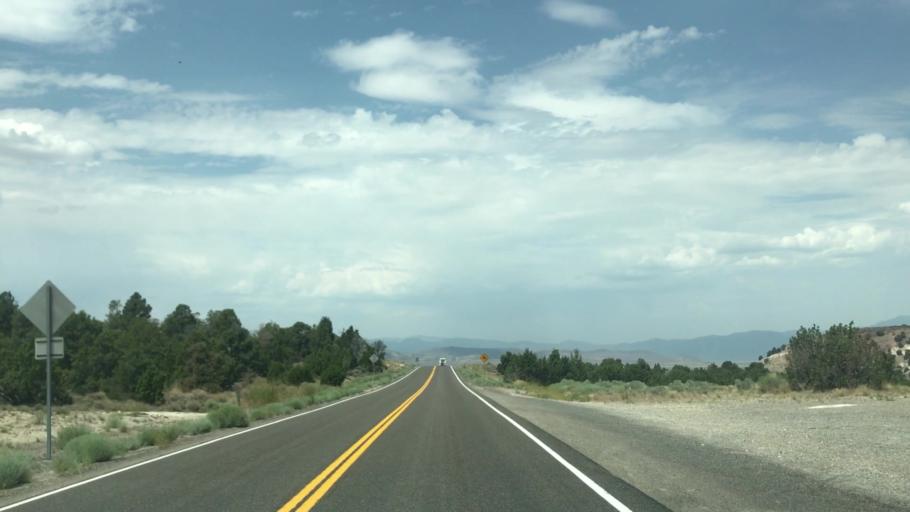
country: US
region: Nevada
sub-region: Eureka County
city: Eureka
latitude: 39.3914
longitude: -115.5051
